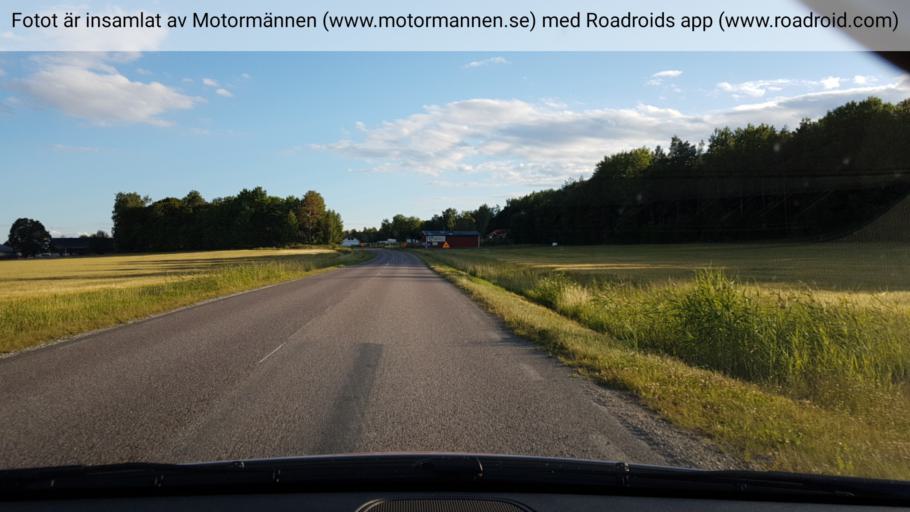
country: SE
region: Vaestmanland
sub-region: Vasteras
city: Tillberga
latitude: 59.6489
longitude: 16.6846
